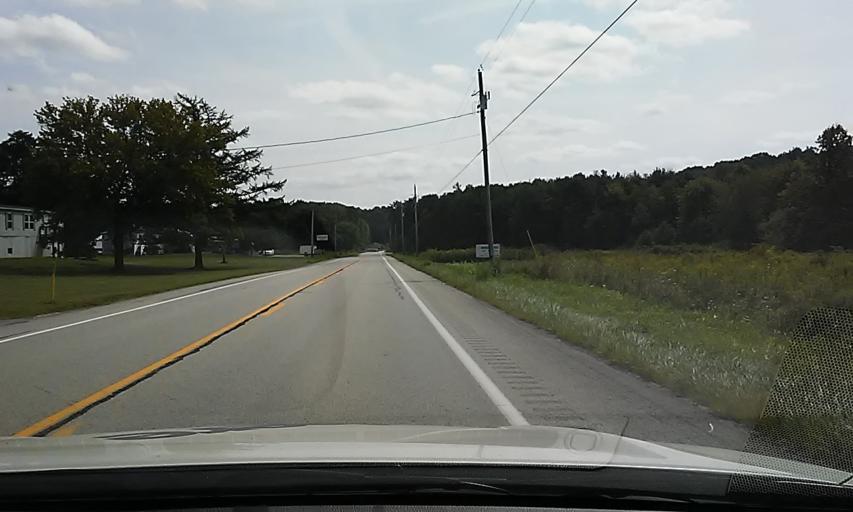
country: US
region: Pennsylvania
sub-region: Indiana County
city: Clymer
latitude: 40.7869
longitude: -79.0541
